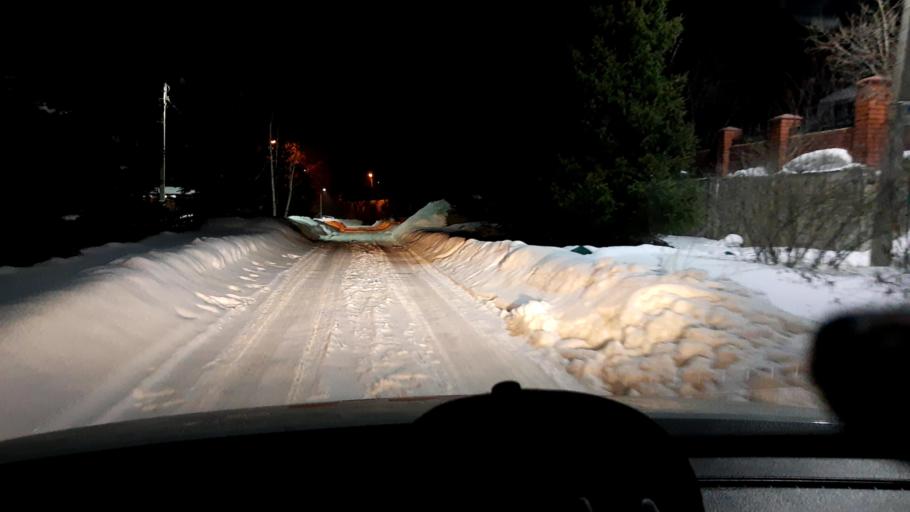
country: RU
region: Bashkortostan
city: Mikhaylovka
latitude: 54.8163
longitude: 55.9009
